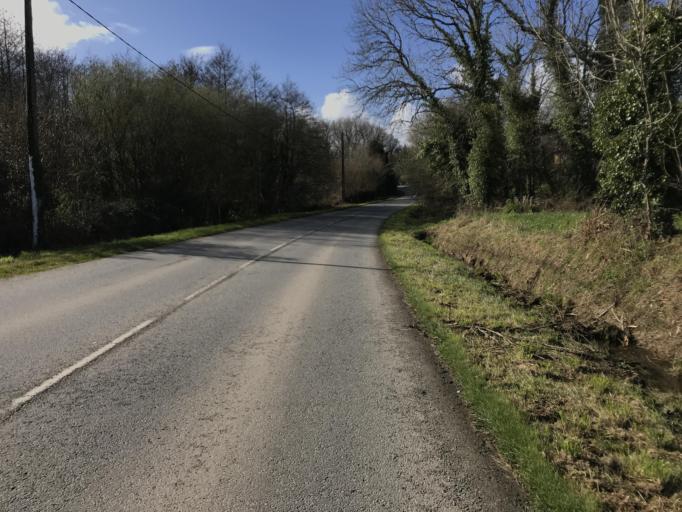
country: FR
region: Brittany
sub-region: Departement du Finistere
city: Loperhet
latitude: 48.3782
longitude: -4.3197
